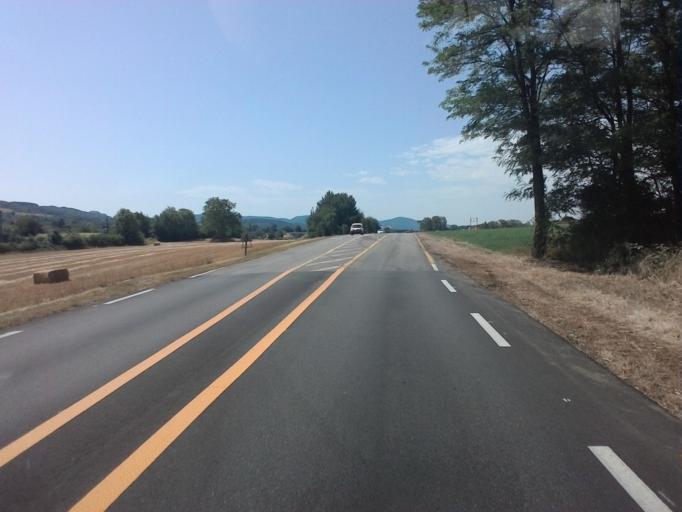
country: FR
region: Franche-Comte
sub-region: Departement du Jura
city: Montmorot
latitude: 46.6495
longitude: 5.5075
